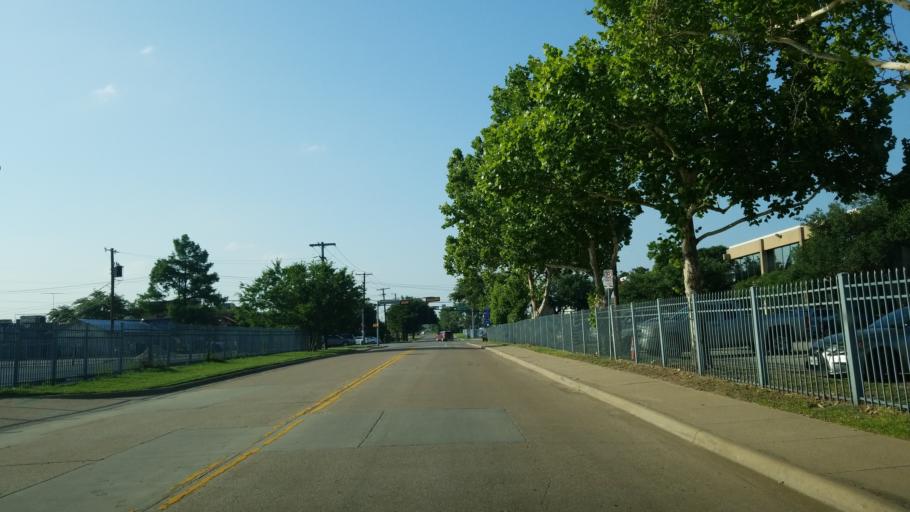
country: US
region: Texas
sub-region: Dallas County
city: Farmers Branch
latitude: 32.8800
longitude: -96.8943
